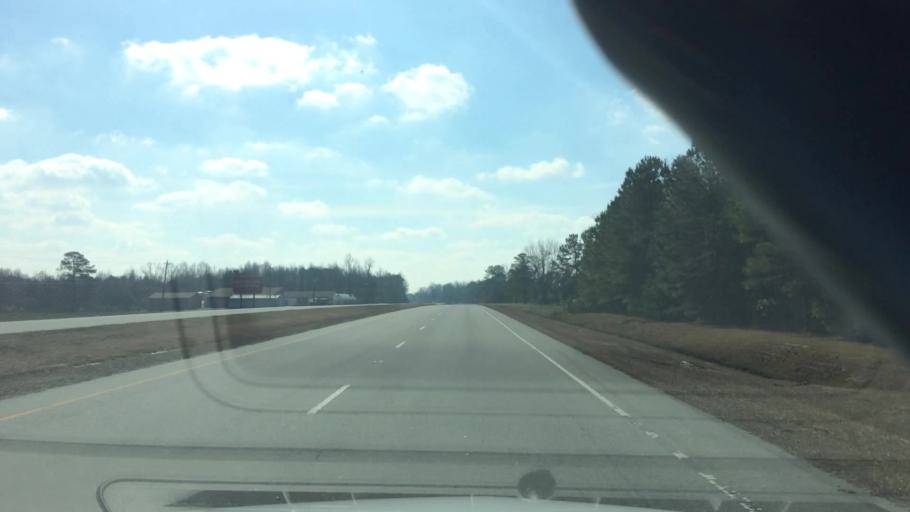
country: US
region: North Carolina
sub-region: Duplin County
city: Beulaville
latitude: 35.0912
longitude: -77.7279
